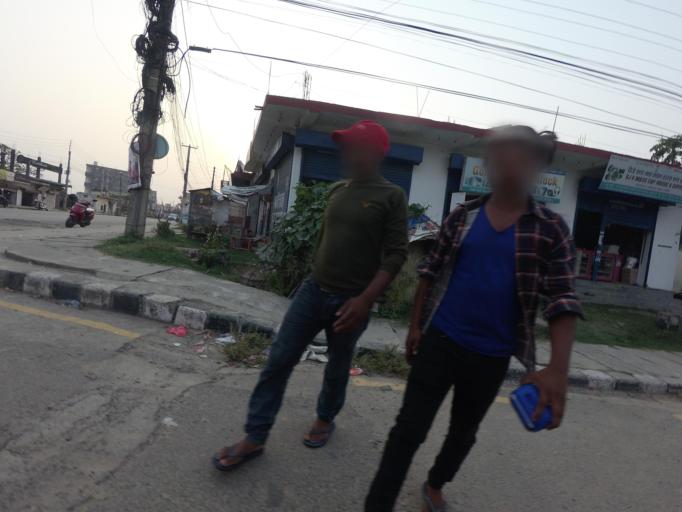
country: NP
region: Western Region
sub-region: Lumbini Zone
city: Bhairahawa
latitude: 27.5058
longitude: 83.4625
